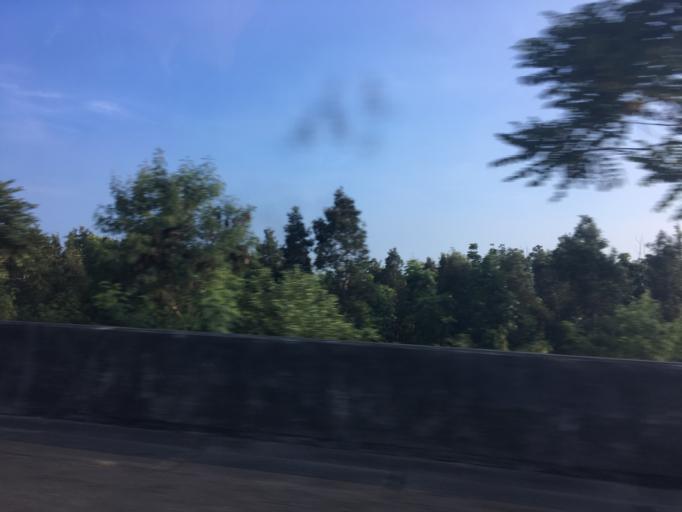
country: TW
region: Taiwan
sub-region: Chiayi
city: Taibao
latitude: 23.4274
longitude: 120.3425
